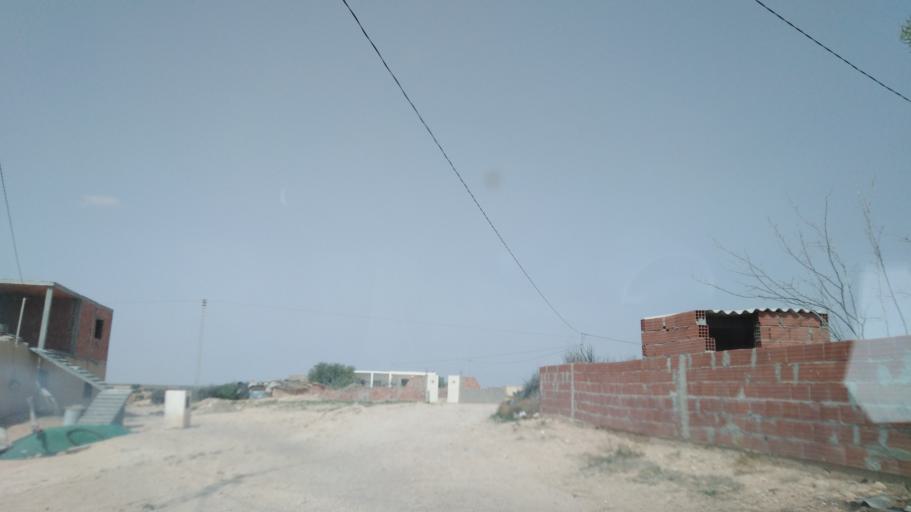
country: TN
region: Safaqis
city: Sfax
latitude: 34.6417
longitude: 10.5613
